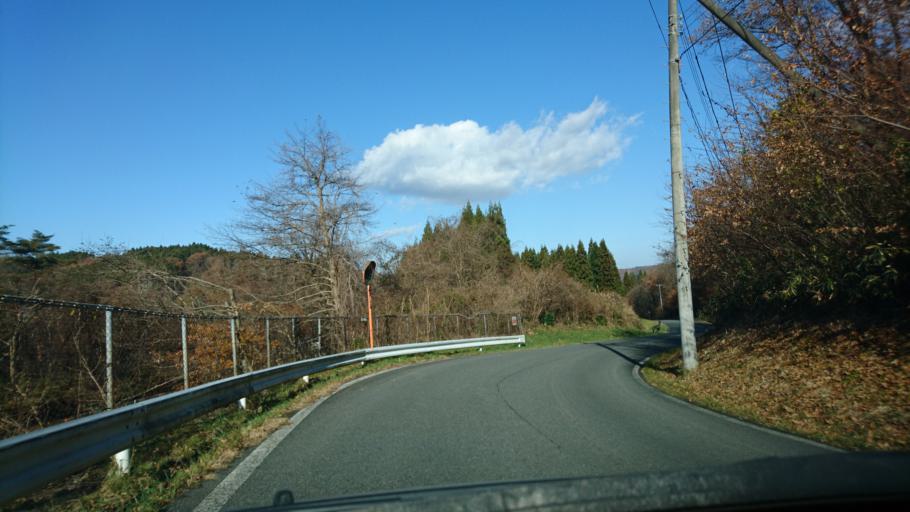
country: JP
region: Iwate
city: Ichinoseki
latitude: 38.9986
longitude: 141.0907
